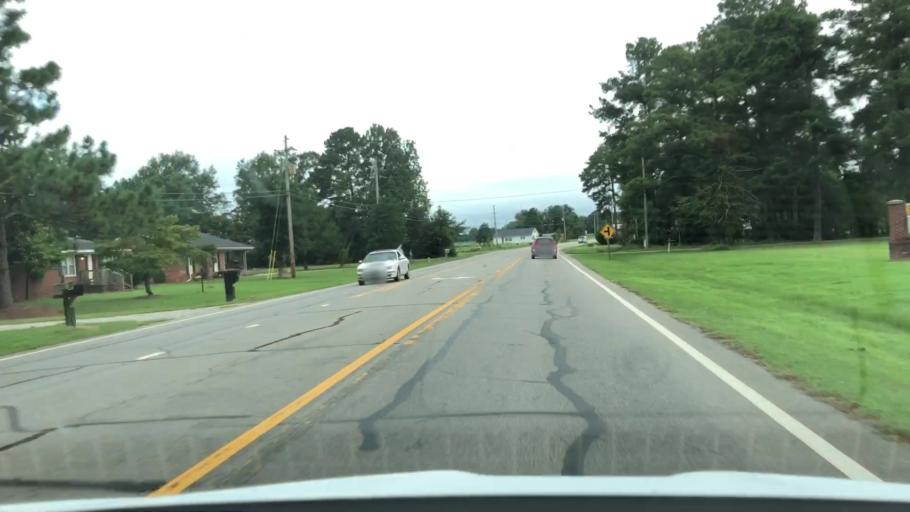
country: US
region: North Carolina
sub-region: Lenoir County
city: Kinston
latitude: 35.2072
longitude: -77.5655
